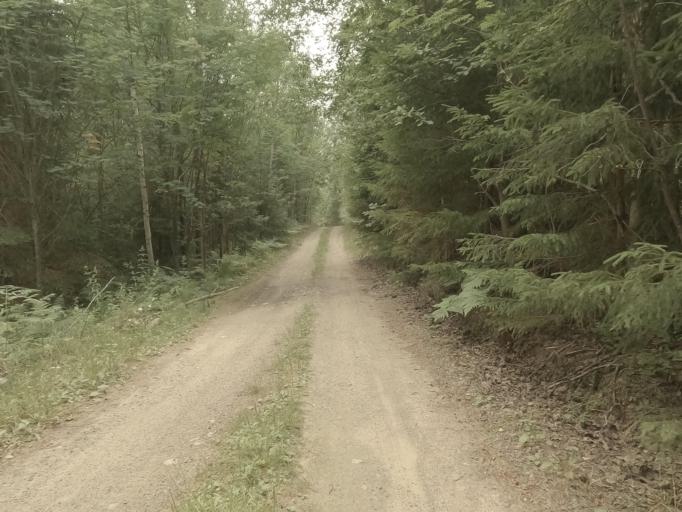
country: RU
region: Leningrad
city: Kamennogorsk
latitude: 61.0120
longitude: 29.2002
